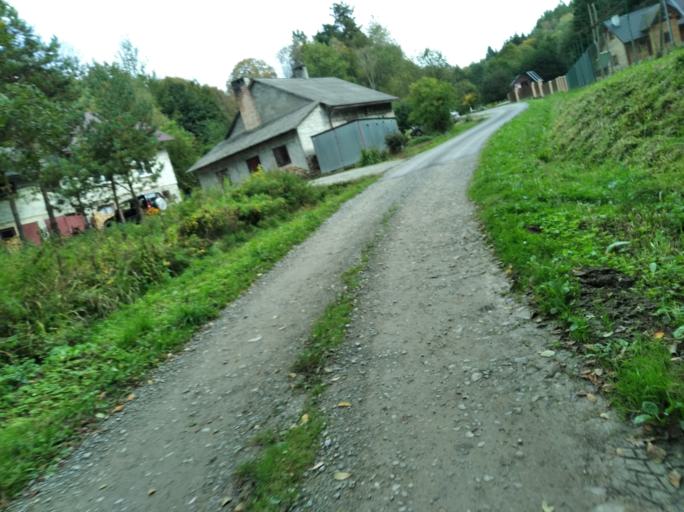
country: PL
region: Subcarpathian Voivodeship
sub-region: Powiat strzyzowski
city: Jawornik
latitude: 49.8322
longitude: 21.8962
